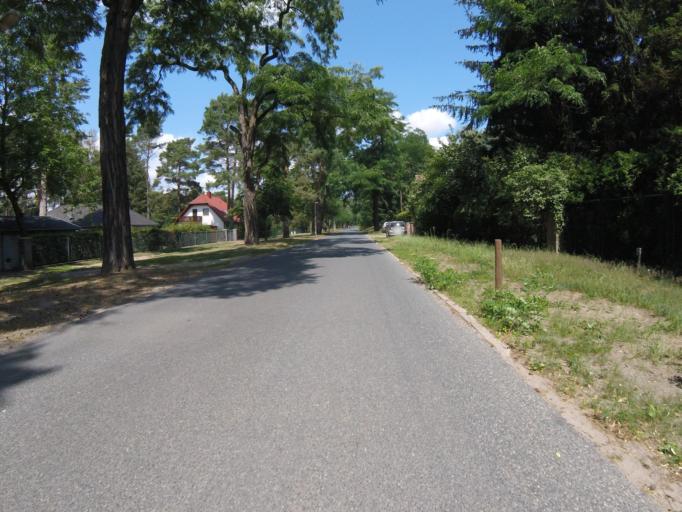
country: DE
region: Brandenburg
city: Bestensee
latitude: 52.2782
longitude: 13.6574
